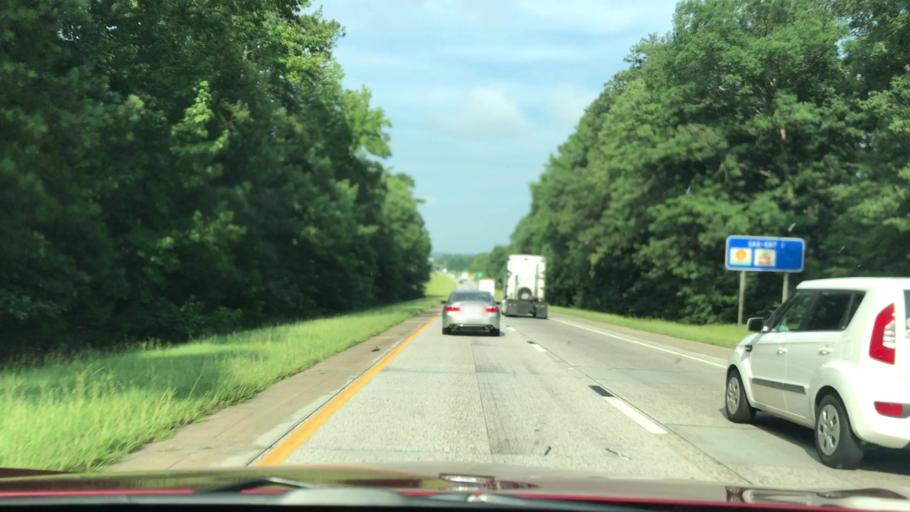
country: US
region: South Carolina
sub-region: Aiken County
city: Belvedere
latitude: 33.5431
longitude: -81.9811
